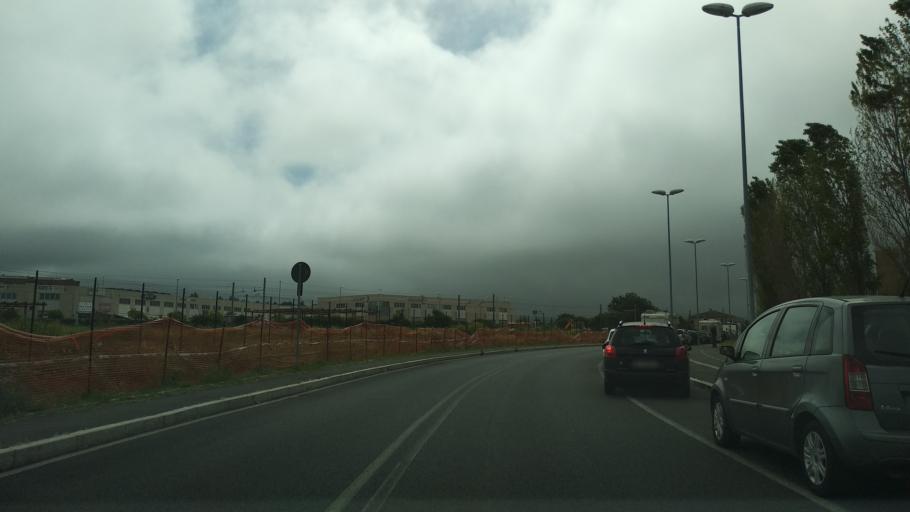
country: IT
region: Tuscany
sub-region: Provincia di Livorno
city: Livorno
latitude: 43.5385
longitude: 10.3322
